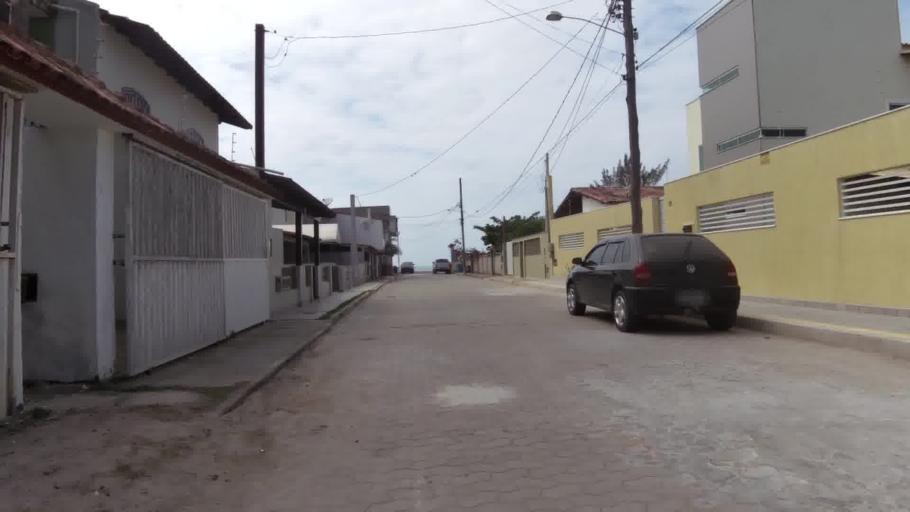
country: BR
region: Espirito Santo
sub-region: Marataizes
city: Marataizes
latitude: -21.0264
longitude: -40.8130
